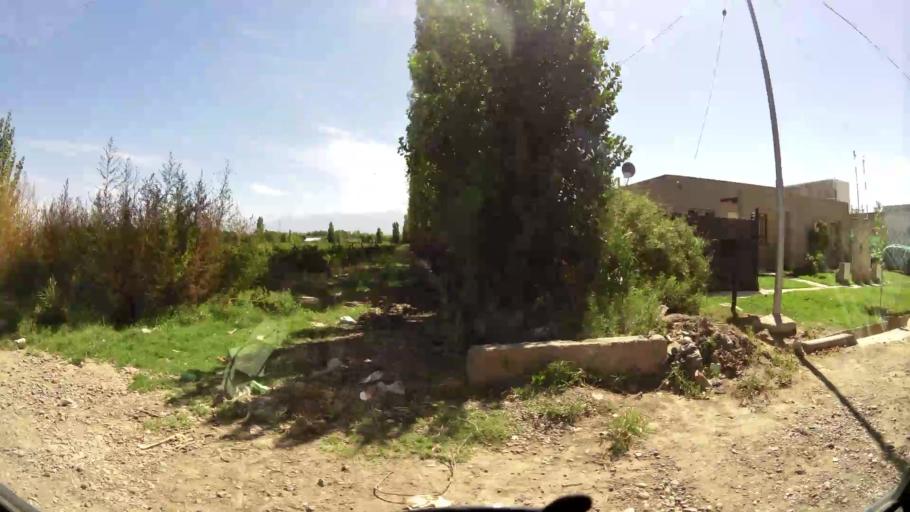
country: AR
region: Mendoza
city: Lujan de Cuyo
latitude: -32.9863
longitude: -68.8508
